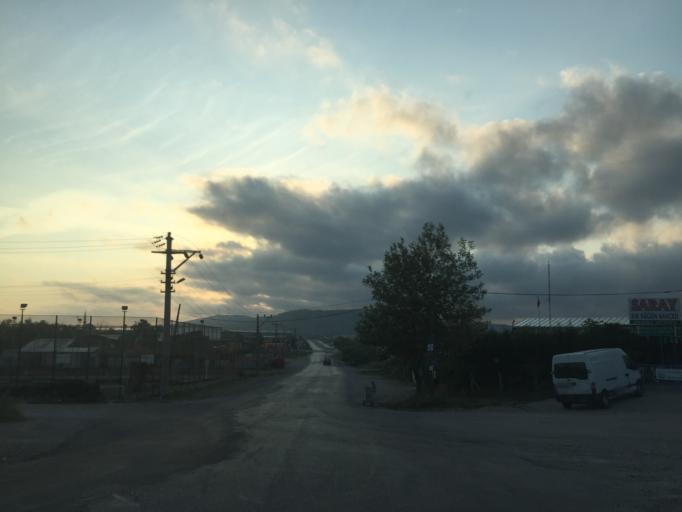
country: TR
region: Balikesir
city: Gonen
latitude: 40.0971
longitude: 27.6642
